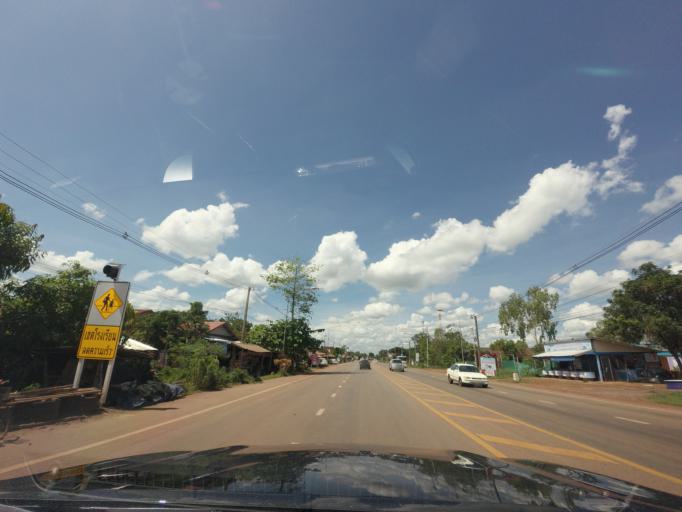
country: TH
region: Changwat Udon Thani
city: Ban Dung
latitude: 17.7072
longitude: 103.2512
